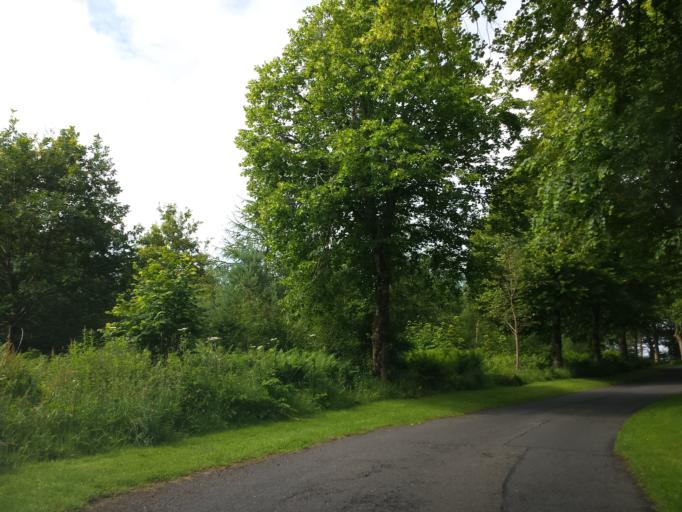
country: GB
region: Scotland
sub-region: South Ayrshire
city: Maybole
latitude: 55.3518
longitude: -4.7744
